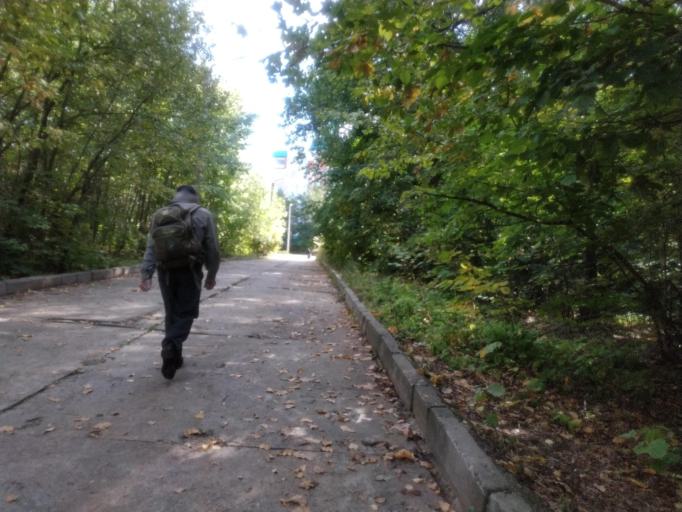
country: RU
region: Chuvashia
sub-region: Cheboksarskiy Rayon
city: Cheboksary
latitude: 56.1533
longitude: 47.1652
